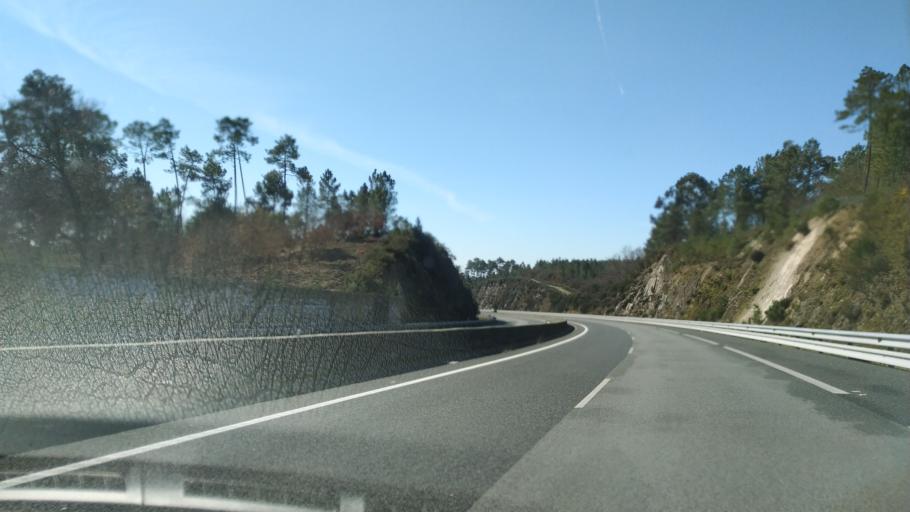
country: ES
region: Galicia
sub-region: Provincia de Ourense
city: Pinor
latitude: 42.5025
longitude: -8.0270
